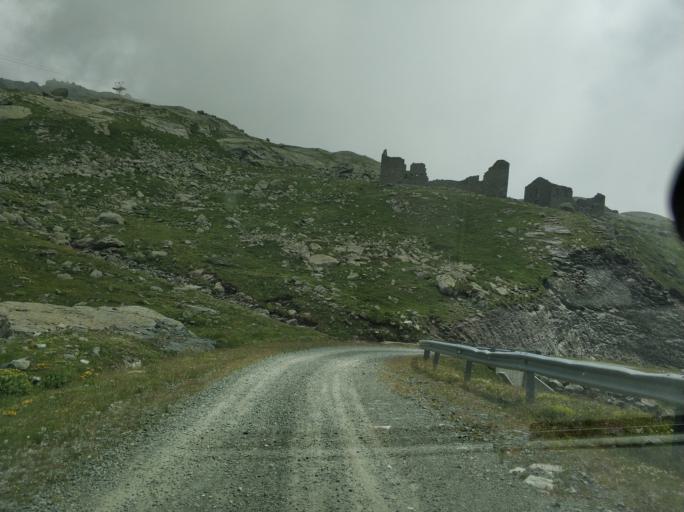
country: IT
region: Piedmont
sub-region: Provincia di Torino
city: Usseglio
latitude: 45.2594
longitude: 7.1655
